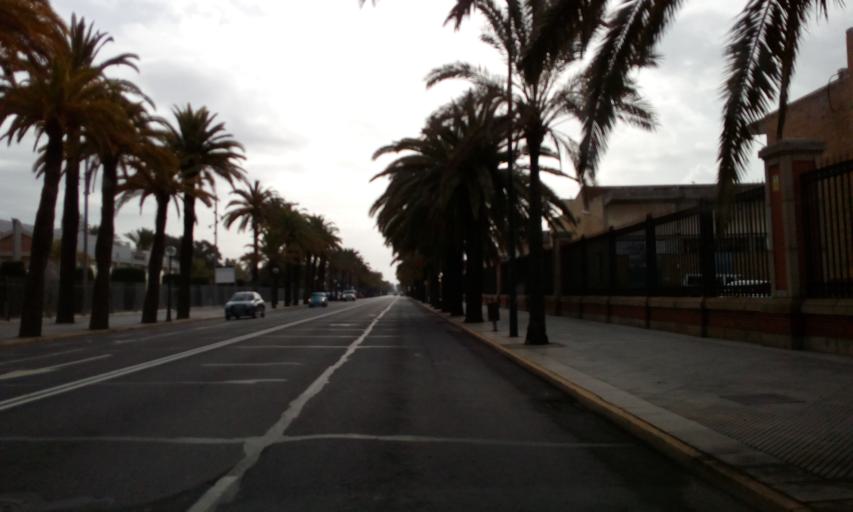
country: ES
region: Andalusia
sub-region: Provincia de Huelva
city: Huelva
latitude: 37.2599
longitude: -6.9611
